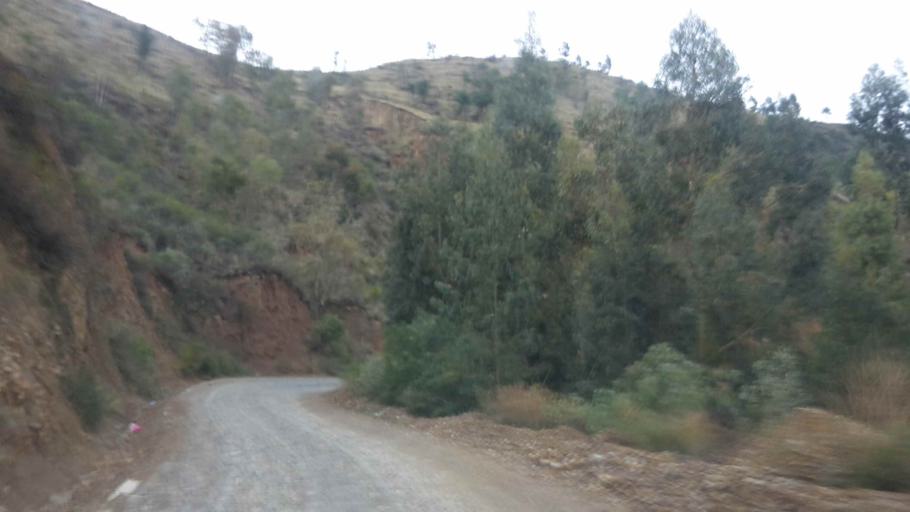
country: BO
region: Cochabamba
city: Cochabamba
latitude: -17.3641
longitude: -66.0635
